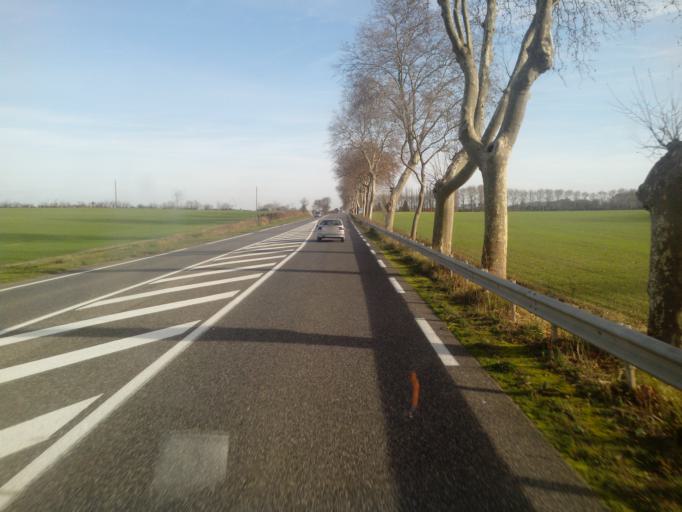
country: FR
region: Languedoc-Roussillon
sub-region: Departement de l'Aude
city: Saint-Martin-Lalande
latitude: 43.2970
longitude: 2.0001
